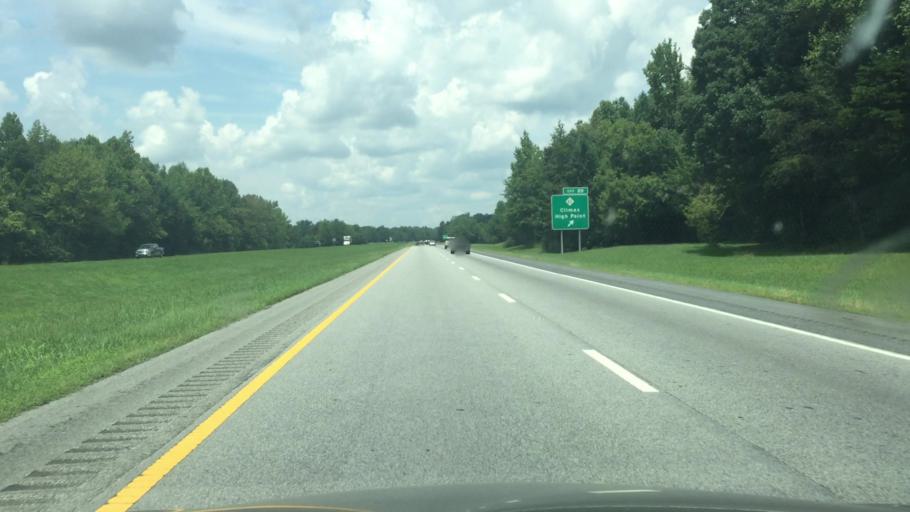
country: US
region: North Carolina
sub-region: Guilford County
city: Pleasant Garden
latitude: 35.9162
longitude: -79.8234
